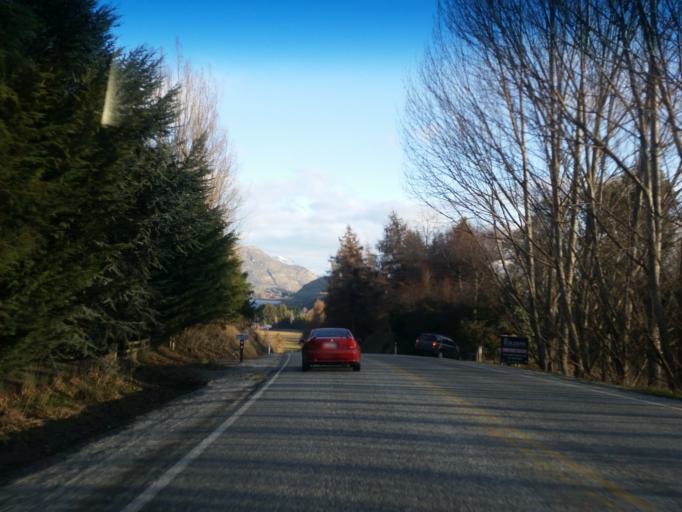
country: NZ
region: Otago
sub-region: Queenstown-Lakes District
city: Arrowtown
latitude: -44.9526
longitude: 168.8198
